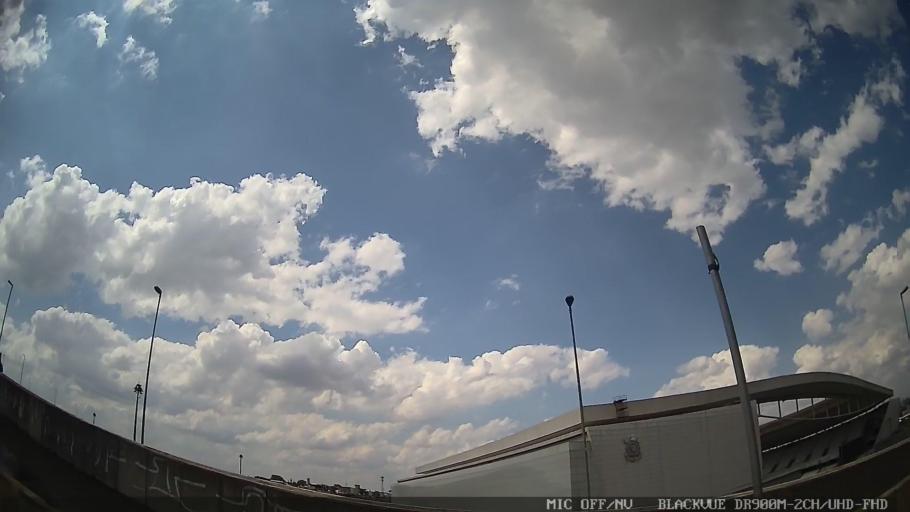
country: BR
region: Sao Paulo
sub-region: Guarulhos
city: Guarulhos
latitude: -23.5472
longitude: -46.4755
